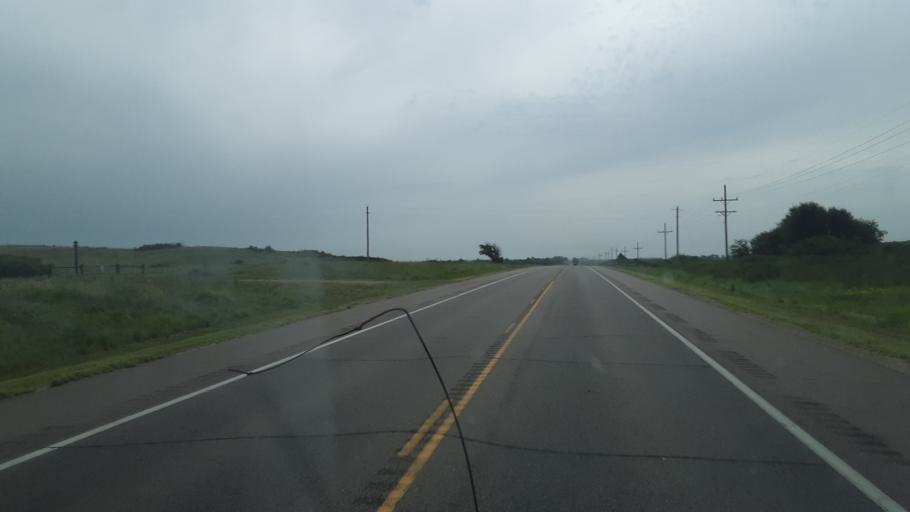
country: US
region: Kansas
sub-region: Edwards County
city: Kinsley
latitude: 37.9275
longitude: -99.3405
